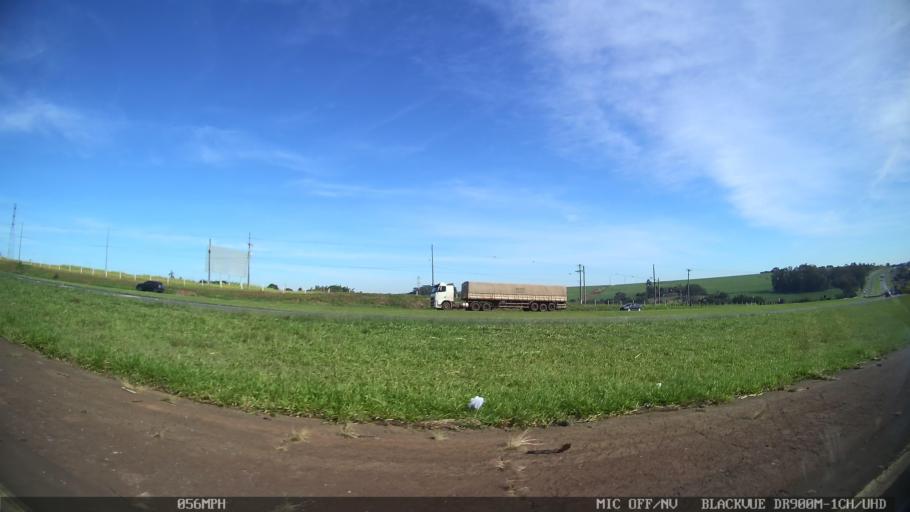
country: BR
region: Sao Paulo
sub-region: Araras
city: Araras
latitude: -22.3988
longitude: -47.3896
